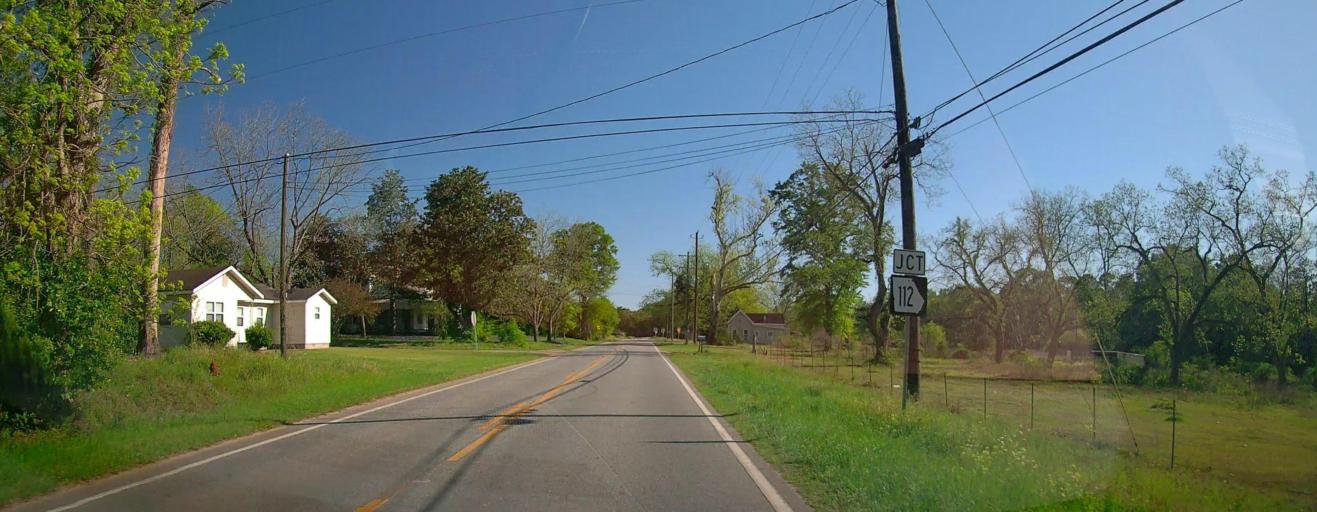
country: US
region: Georgia
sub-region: Wilcox County
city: Rochelle
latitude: 31.9394
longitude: -83.4564
